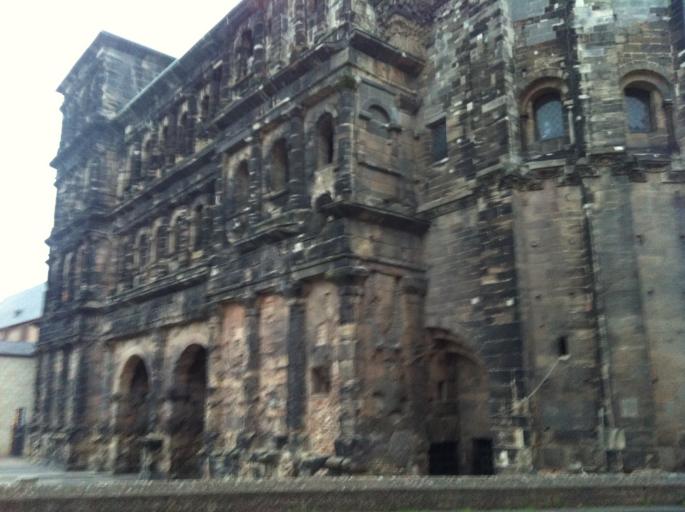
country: DE
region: Rheinland-Pfalz
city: Trier
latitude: 49.7593
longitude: 6.6442
